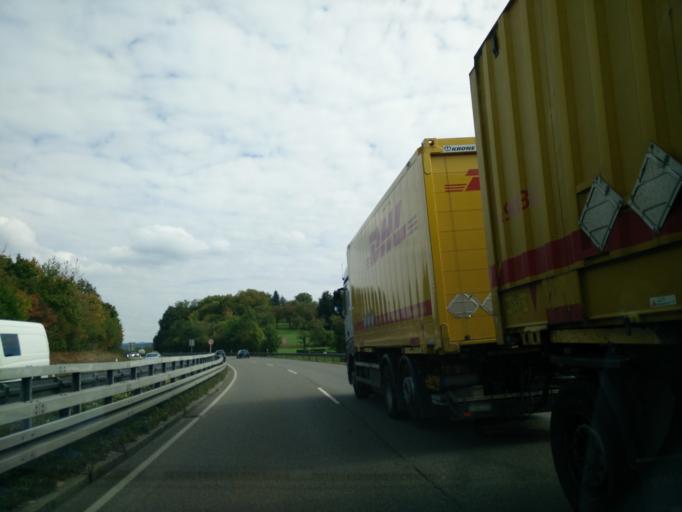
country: DE
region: Baden-Wuerttemberg
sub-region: Tuebingen Region
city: Reutlingen
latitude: 48.4932
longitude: 9.1736
